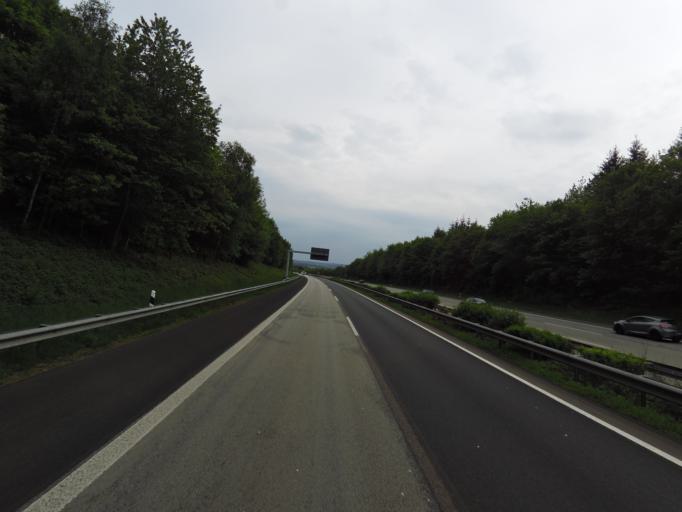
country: DE
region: Rheinland-Pfalz
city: Nortershausen
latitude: 50.2316
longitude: 7.5170
